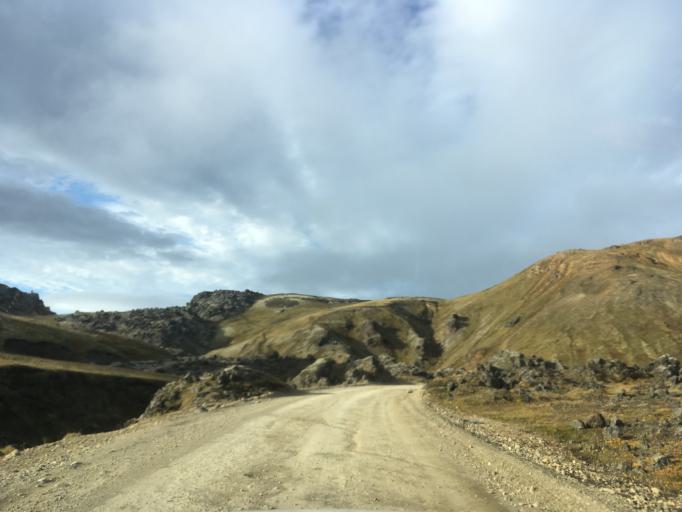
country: IS
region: South
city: Vestmannaeyjar
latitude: 63.9990
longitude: -19.0512
